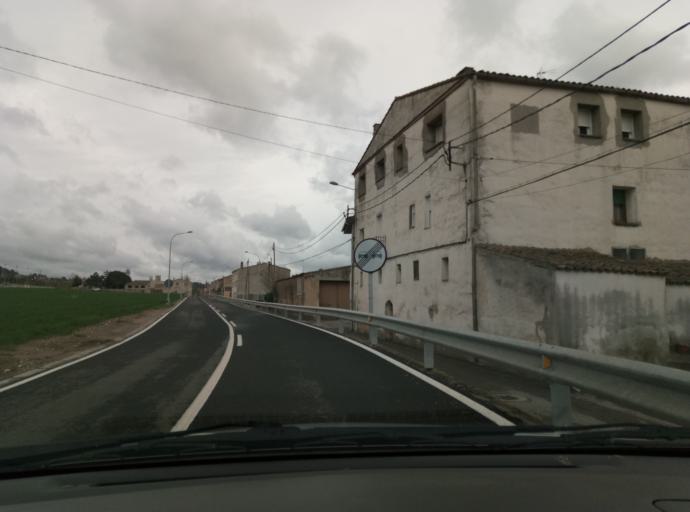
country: ES
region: Catalonia
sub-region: Provincia de Lleida
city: Cervera
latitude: 41.6315
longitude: 1.3386
